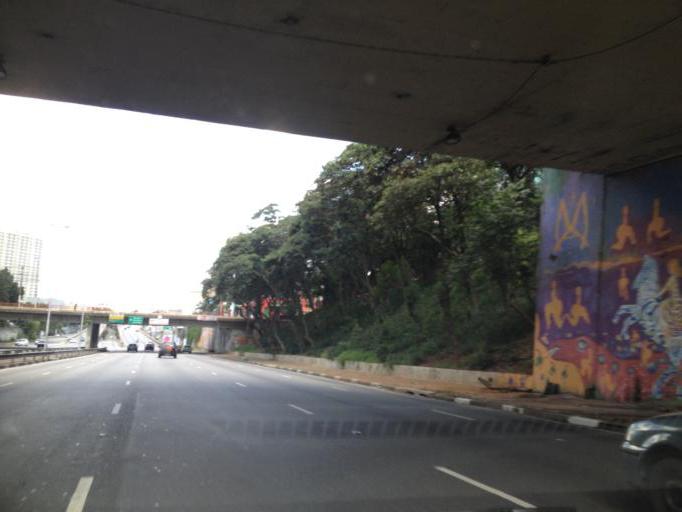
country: BR
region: Sao Paulo
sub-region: Sao Paulo
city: Sao Paulo
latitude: -23.5566
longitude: -46.6343
